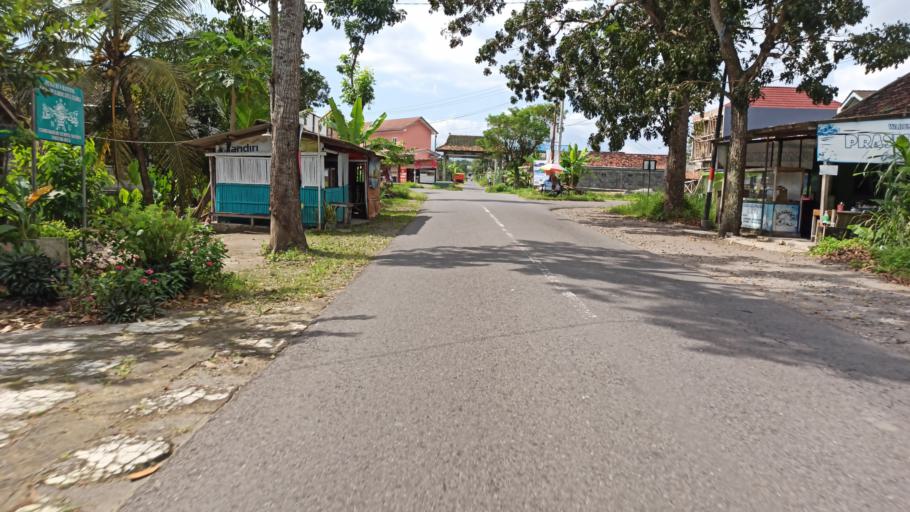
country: ID
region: Daerah Istimewa Yogyakarta
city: Sleman
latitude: -7.6875
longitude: 110.2984
